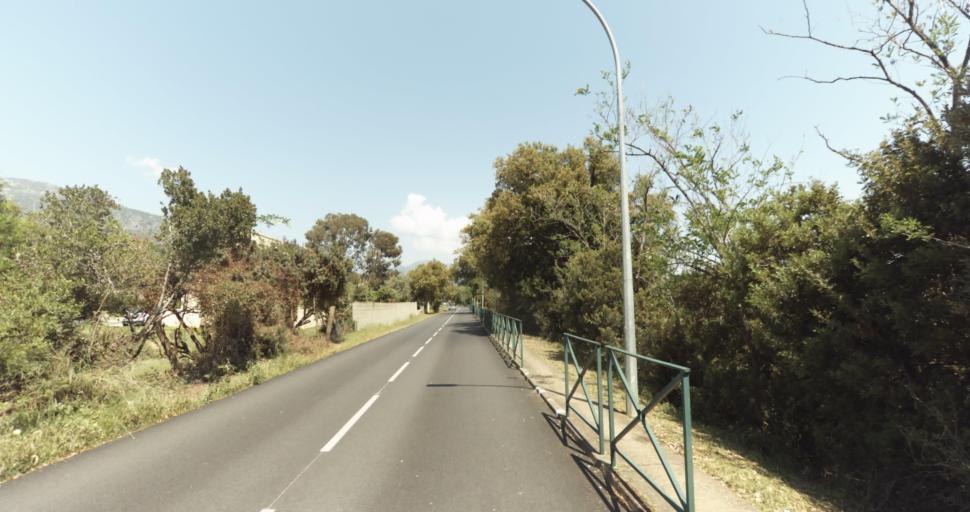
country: FR
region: Corsica
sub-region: Departement de la Haute-Corse
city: Biguglia
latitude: 42.6036
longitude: 9.4342
